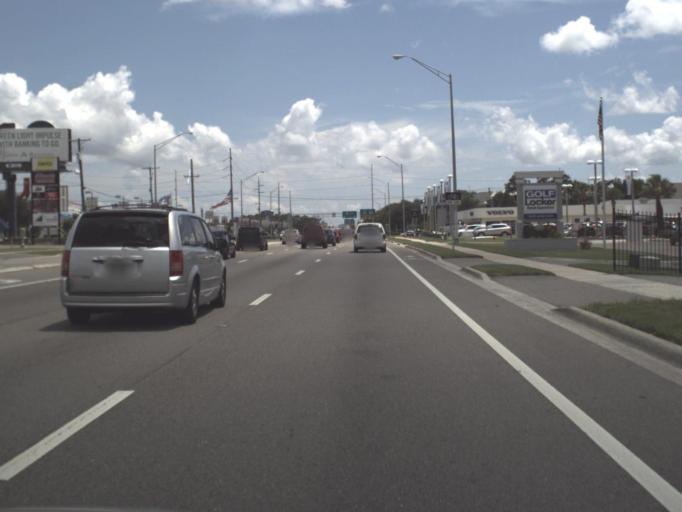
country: US
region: Florida
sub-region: Hillsborough County
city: Egypt Lake-Leto
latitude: 28.0040
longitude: -82.5053
